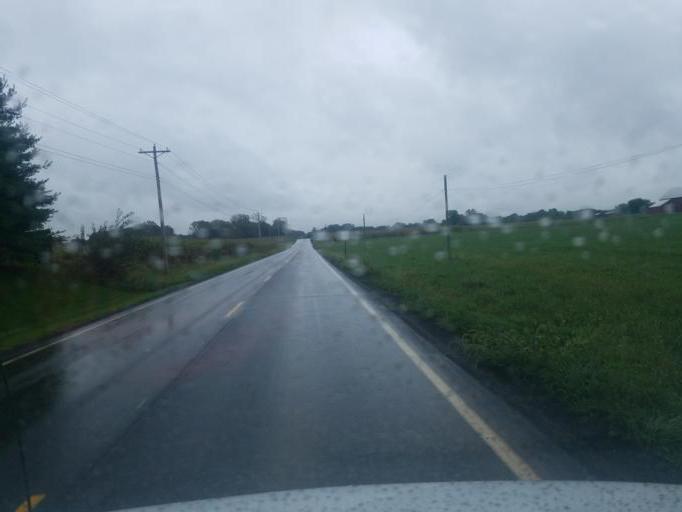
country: US
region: Ohio
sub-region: Wayne County
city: West Salem
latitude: 40.9153
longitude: -82.1230
